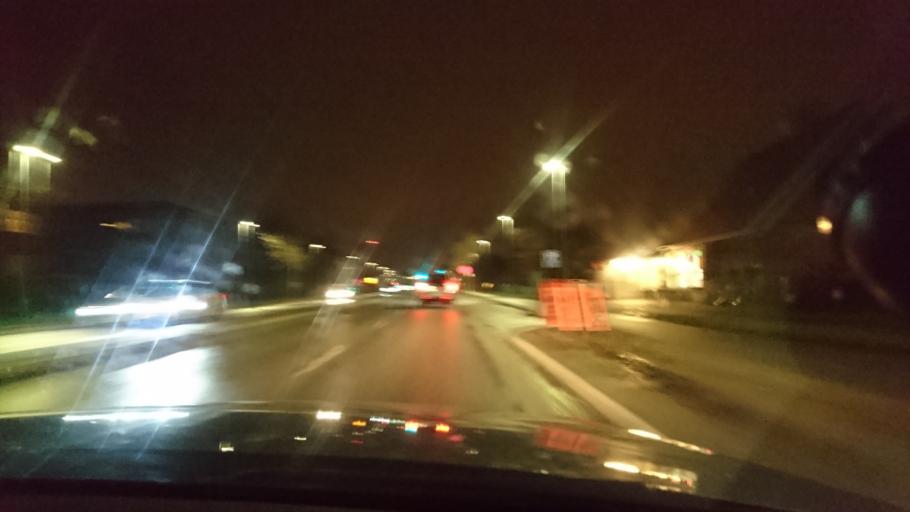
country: DK
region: Capital Region
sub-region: Tarnby Kommune
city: Tarnby
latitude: 55.6369
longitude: 12.6000
